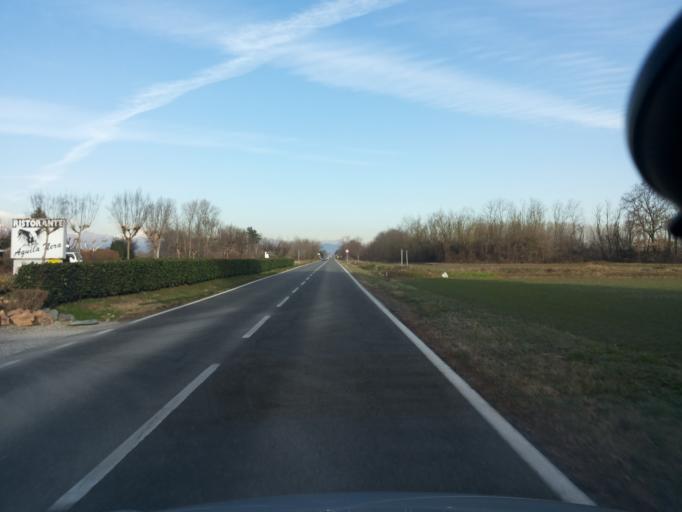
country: IT
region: Piedmont
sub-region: Provincia di Vercelli
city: Arborio
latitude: 45.5096
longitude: 8.3881
